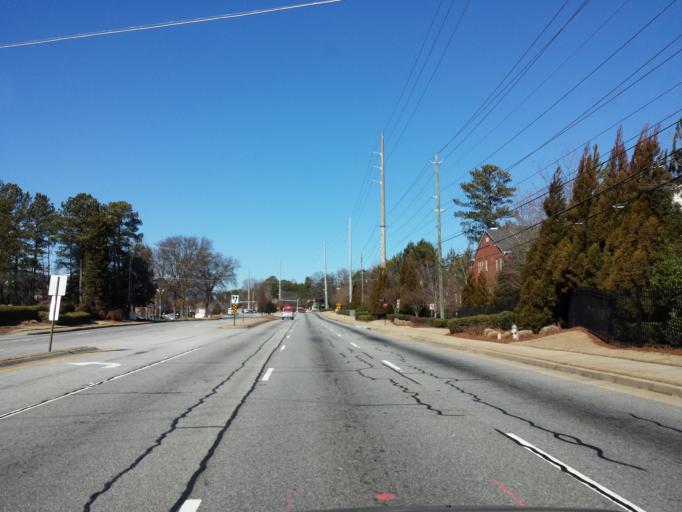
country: US
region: Georgia
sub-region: Cobb County
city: Vinings
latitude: 33.9112
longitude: -84.4651
